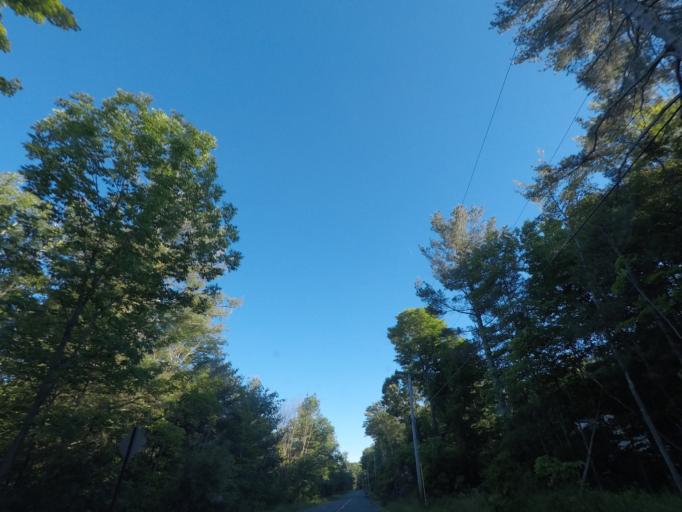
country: US
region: New York
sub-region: Rensselaer County
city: Averill Park
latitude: 42.5711
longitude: -73.5327
